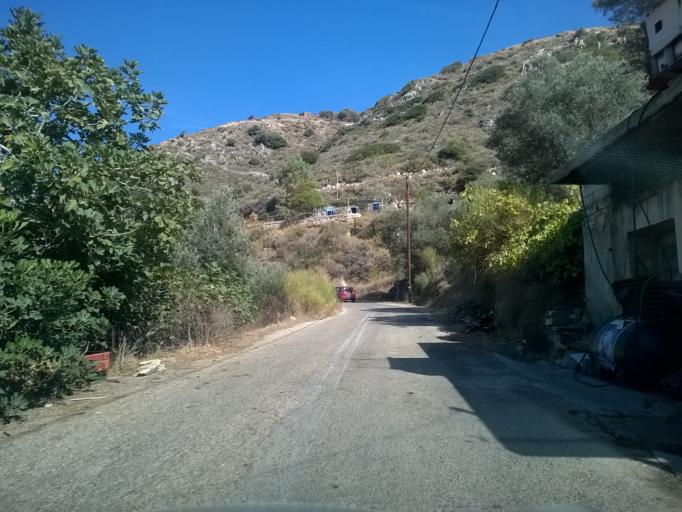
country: GR
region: South Aegean
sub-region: Nomos Kykladon
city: Filotion
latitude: 37.1526
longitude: 25.5486
